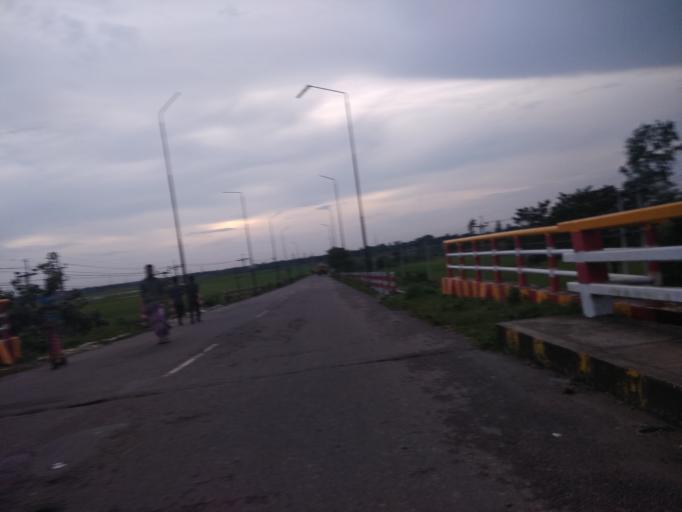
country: BD
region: Dhaka
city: Azimpur
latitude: 23.6687
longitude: 90.2883
